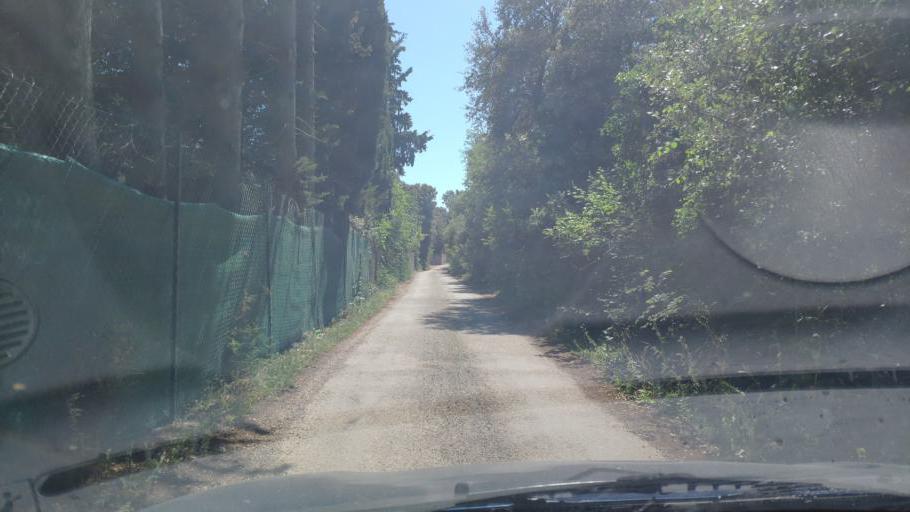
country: FR
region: Provence-Alpes-Cote d'Azur
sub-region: Departement du Vaucluse
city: Carpentras
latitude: 44.0793
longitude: 5.0493
